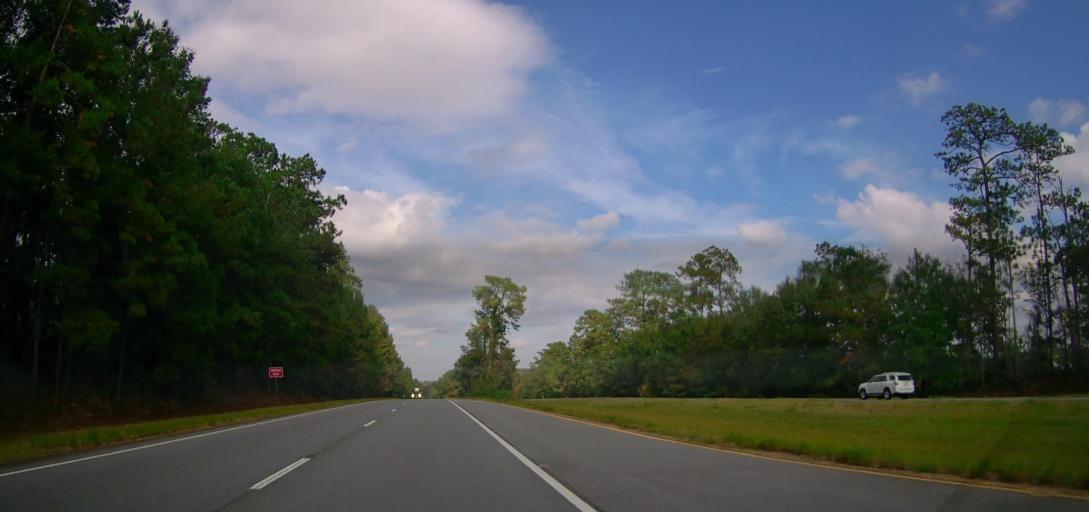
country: US
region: Georgia
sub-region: Thomas County
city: Thomasville
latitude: 30.7372
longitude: -84.1124
